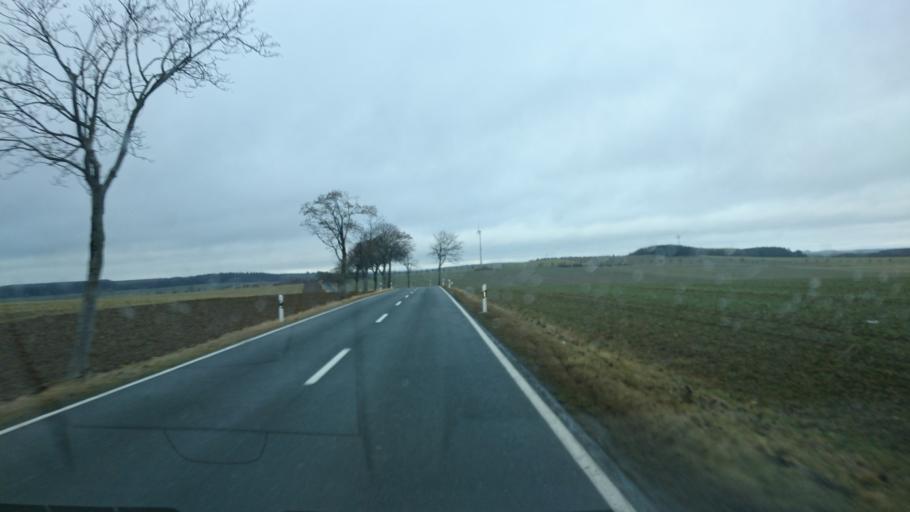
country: DE
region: Thuringia
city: Tanna
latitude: 50.5241
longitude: 11.8802
